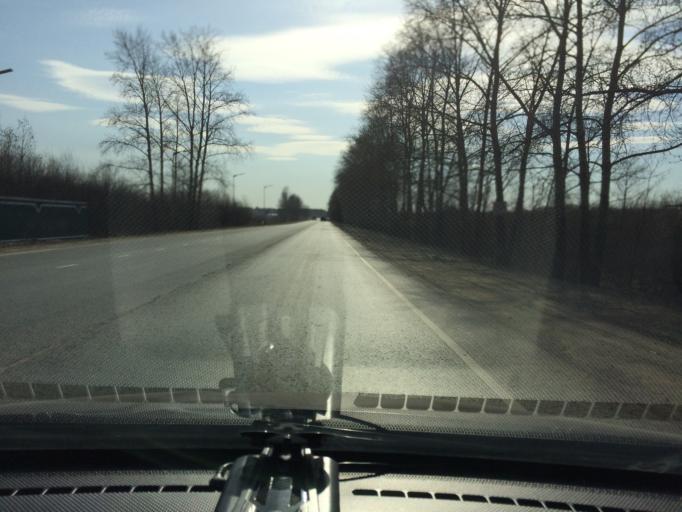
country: RU
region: Mariy-El
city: Yoshkar-Ola
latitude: 56.6530
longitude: 47.9525
